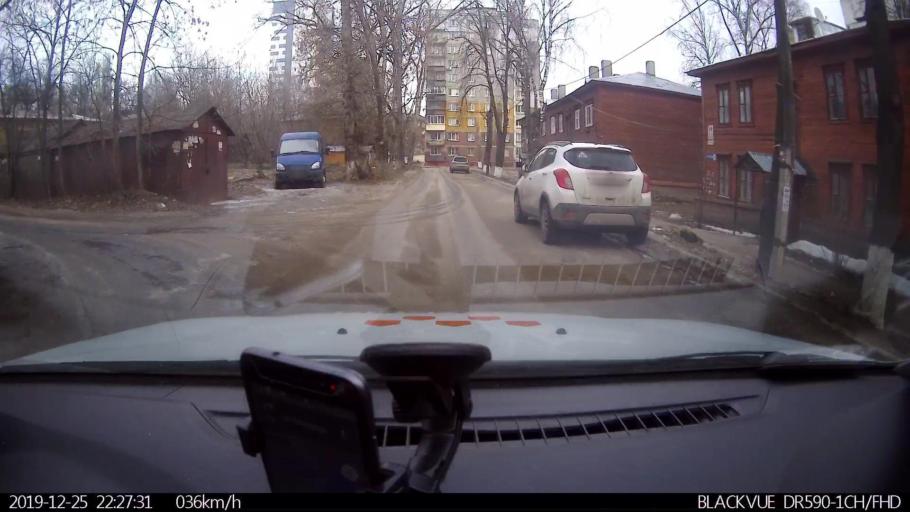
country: RU
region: Nizjnij Novgorod
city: Nizhniy Novgorod
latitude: 56.2646
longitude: 43.9765
